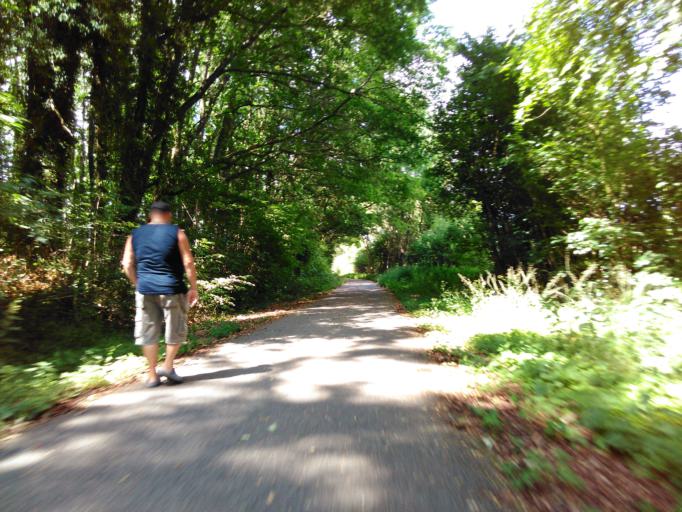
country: LU
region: Luxembourg
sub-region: Canton de Capellen
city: Clemency
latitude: 49.6116
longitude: 5.8774
